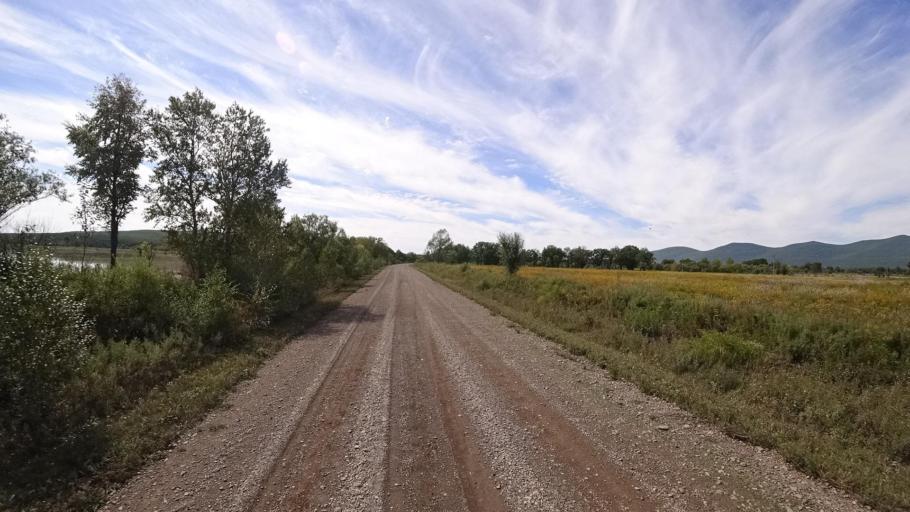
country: RU
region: Primorskiy
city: Kirovskiy
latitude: 44.7715
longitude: 133.6244
